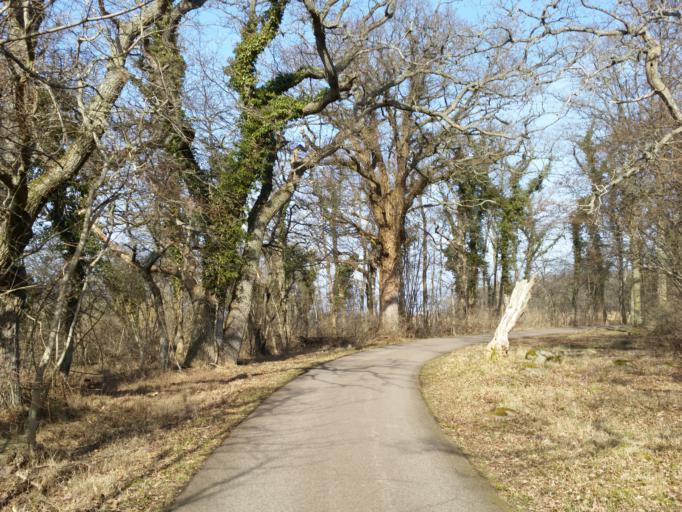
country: SE
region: Kalmar
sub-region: Borgholms Kommun
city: Borgholm
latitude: 56.8757
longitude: 16.6374
